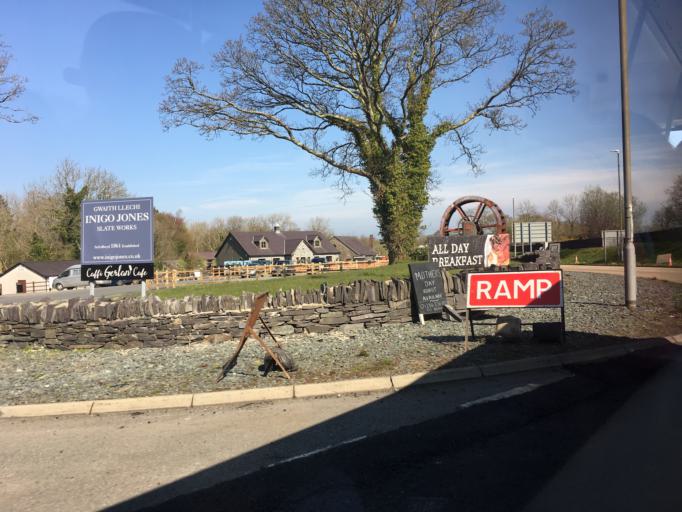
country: GB
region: Wales
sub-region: Gwynedd
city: Llanwnda
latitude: 53.0702
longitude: -4.2837
